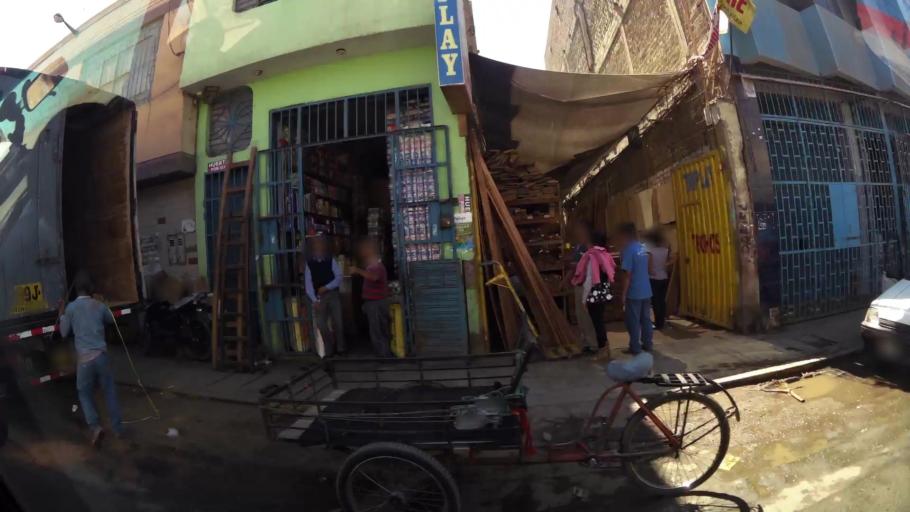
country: PE
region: Ica
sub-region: Provincia de Ica
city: Ica
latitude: -14.0596
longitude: -75.7278
